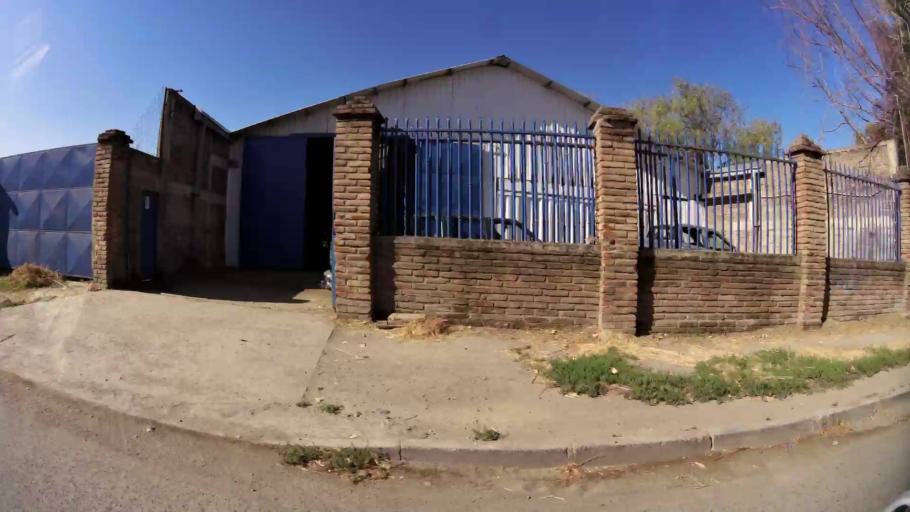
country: CL
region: Maule
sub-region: Provincia de Talca
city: Talca
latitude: -35.3978
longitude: -71.6242
